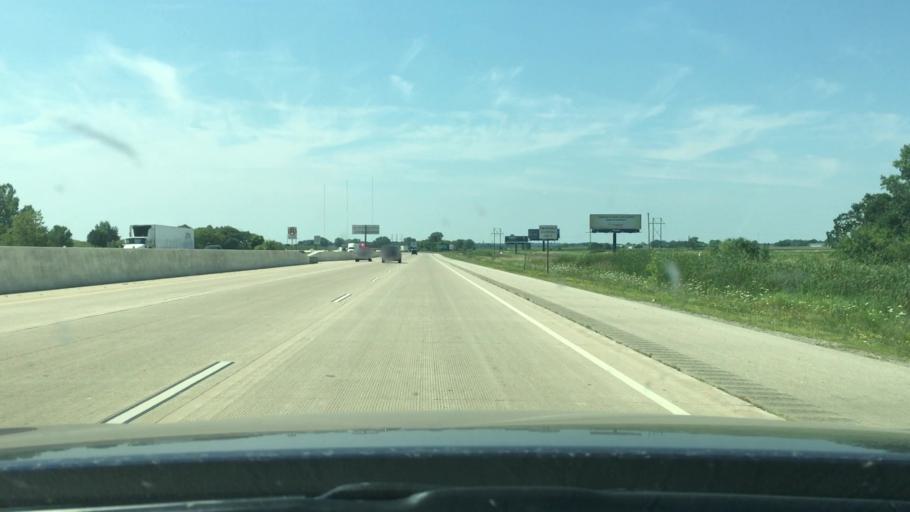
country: US
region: Wisconsin
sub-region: Winnebago County
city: Oshkosh
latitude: 44.0907
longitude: -88.5526
